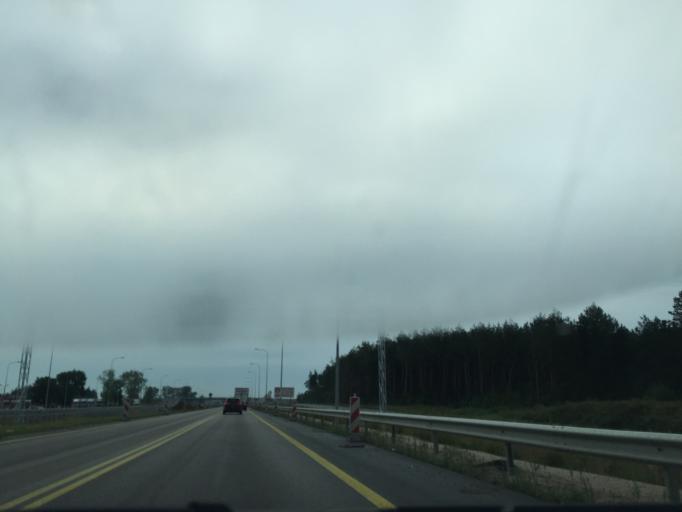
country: PL
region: Podlasie
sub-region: Powiat zambrowski
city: Szumowo
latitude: 52.9064
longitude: 22.0911
